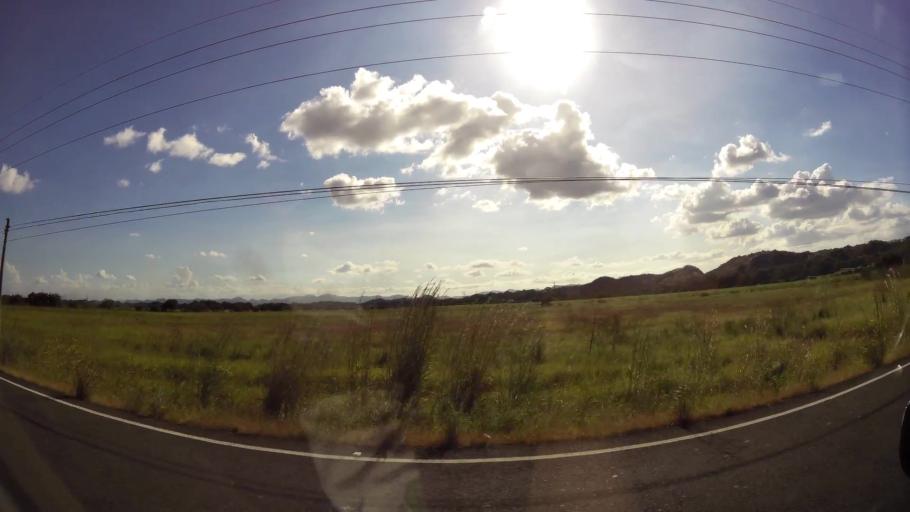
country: CR
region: Guanacaste
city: Sardinal
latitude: 10.5685
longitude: -85.6179
